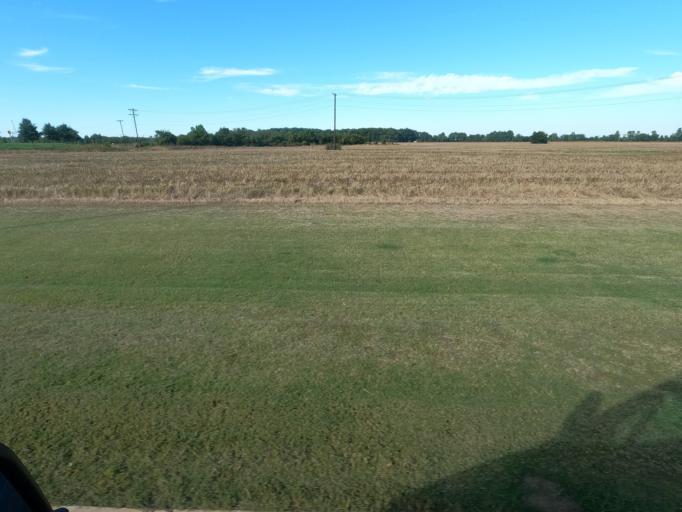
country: US
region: Arkansas
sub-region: Crittenden County
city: West Memphis
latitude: 35.1658
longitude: -90.1724
